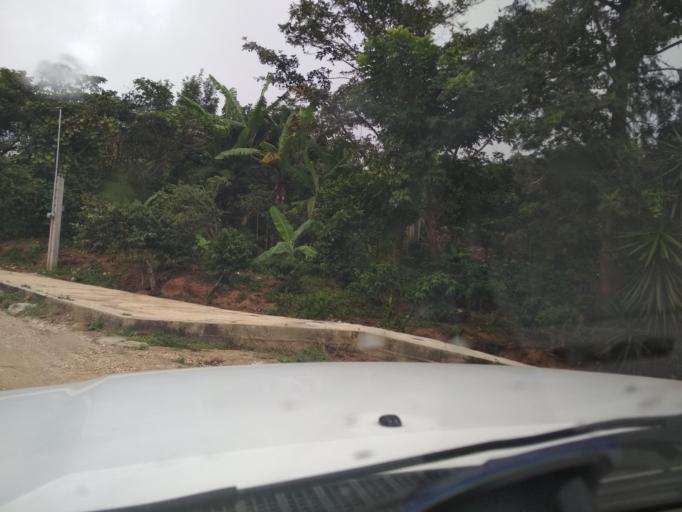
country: MX
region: Veracruz
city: El Castillo
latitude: 19.5430
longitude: -96.8269
